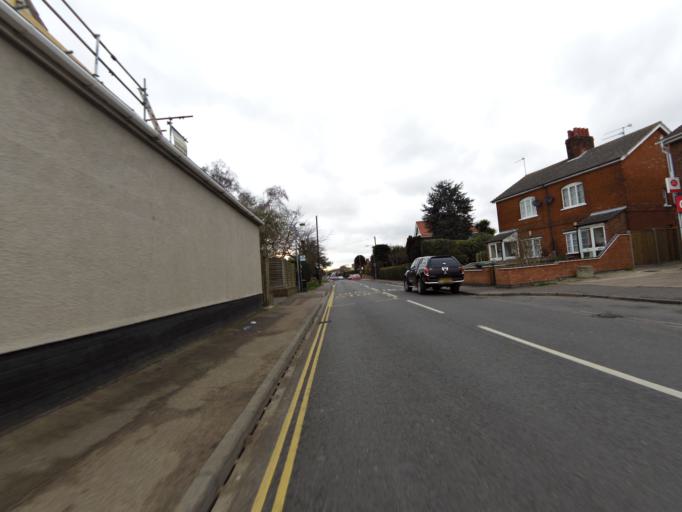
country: GB
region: England
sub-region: Norfolk
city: Hopton on Sea
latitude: 52.5393
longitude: 1.7282
